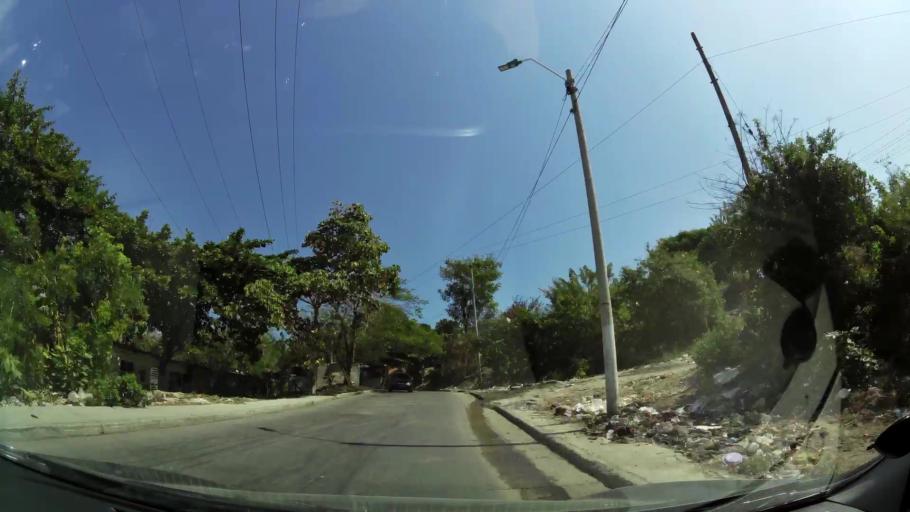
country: CO
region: Atlantico
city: Barranquilla
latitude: 10.9808
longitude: -74.8199
